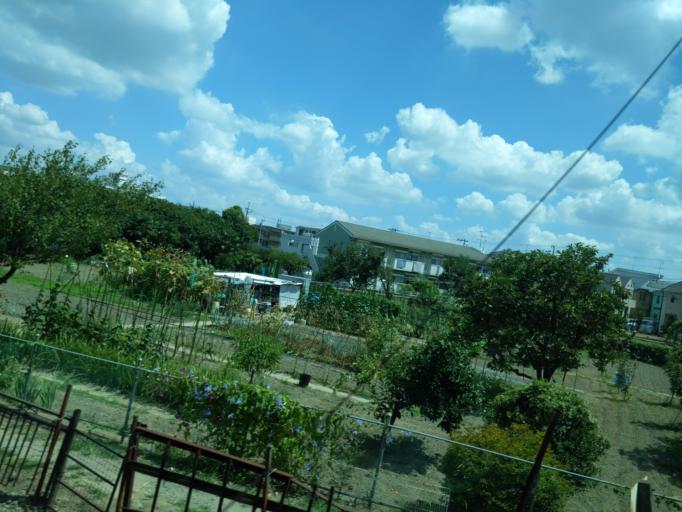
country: JP
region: Tokyo
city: Chofugaoka
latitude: 35.6260
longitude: 139.5595
